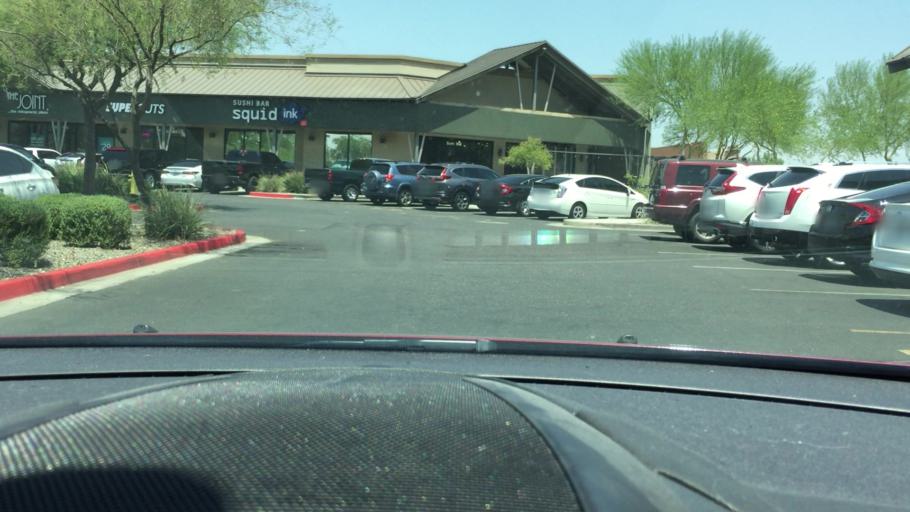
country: US
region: Arizona
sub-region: Maricopa County
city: Sun City West
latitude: 33.7101
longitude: -112.2732
